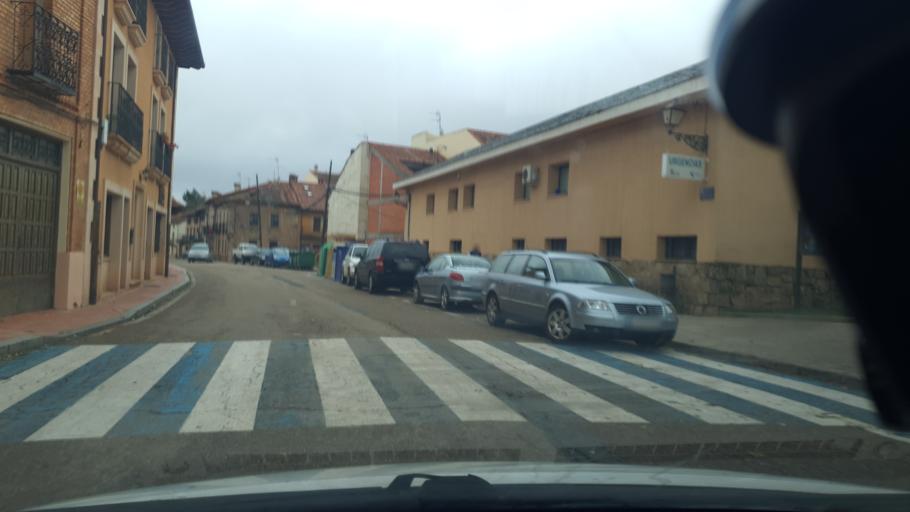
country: ES
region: Castille and Leon
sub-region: Provincia de Segovia
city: Riaza
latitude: 41.2769
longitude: -3.4800
